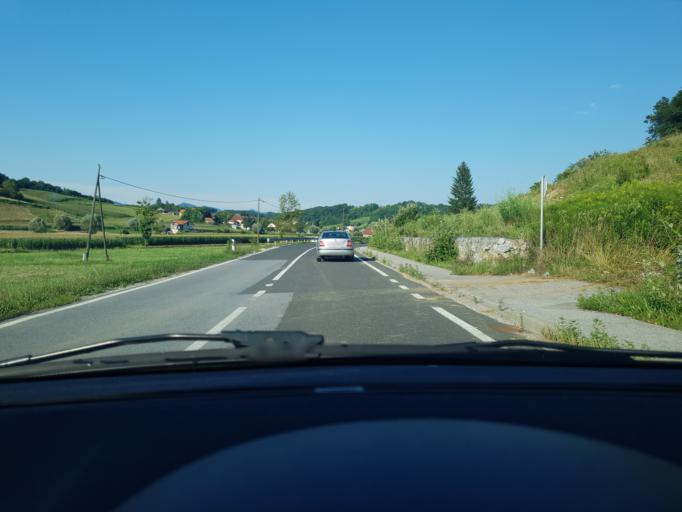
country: HR
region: Krapinsko-Zagorska
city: Radoboj
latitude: 46.1185
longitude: 15.9216
